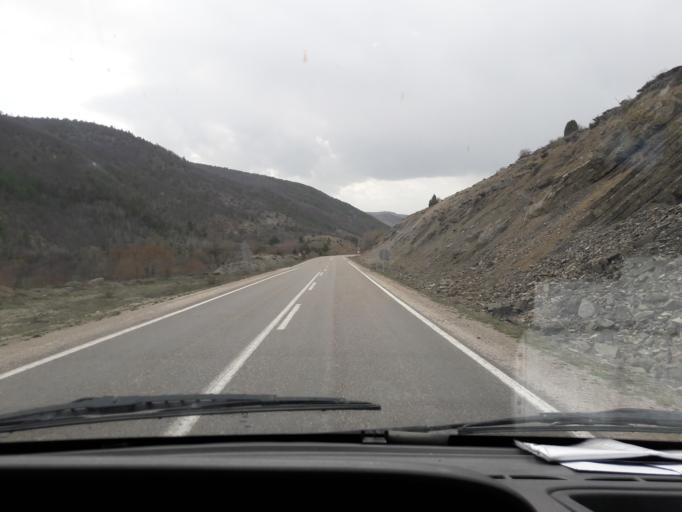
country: TR
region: Giresun
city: Alucra
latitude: 40.2734
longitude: 38.8643
